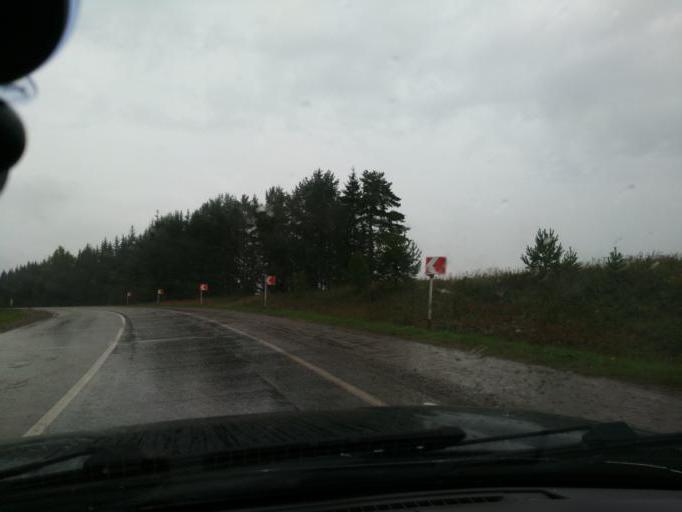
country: RU
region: Perm
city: Osa
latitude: 57.3159
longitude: 55.6235
